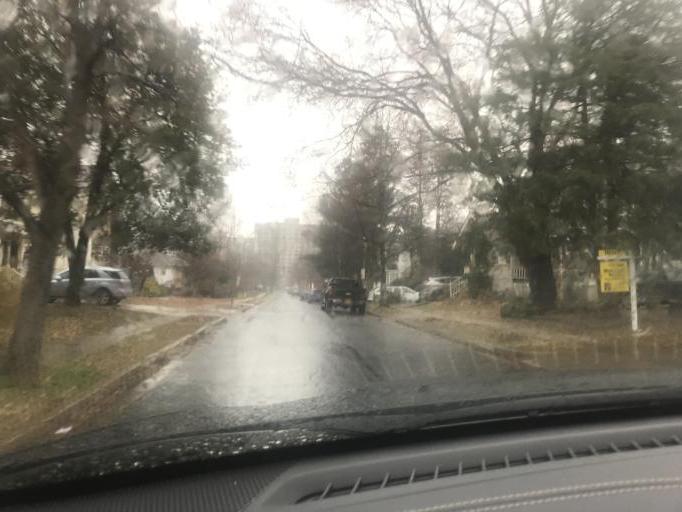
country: US
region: Washington, D.C.
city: Washington, D.C.
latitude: 38.8524
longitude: -77.0564
